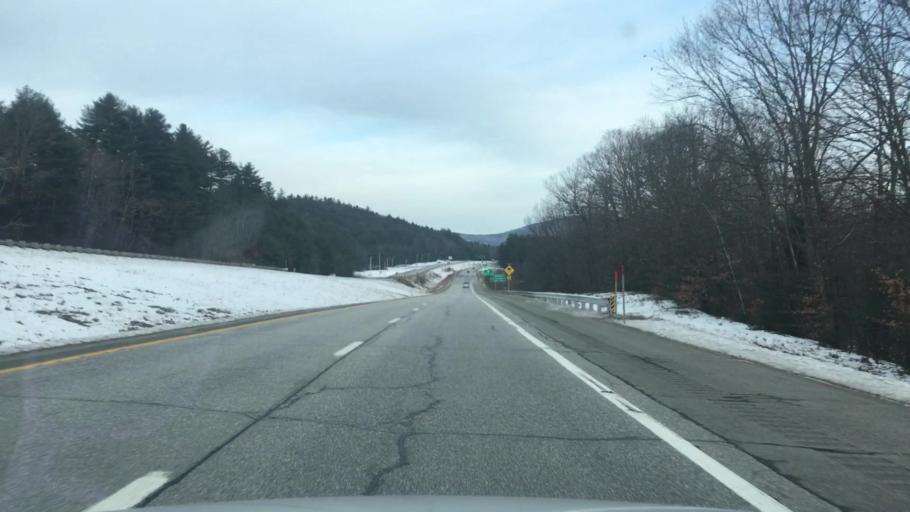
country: US
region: New Hampshire
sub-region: Merrimack County
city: Henniker
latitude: 43.2847
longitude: -71.8337
